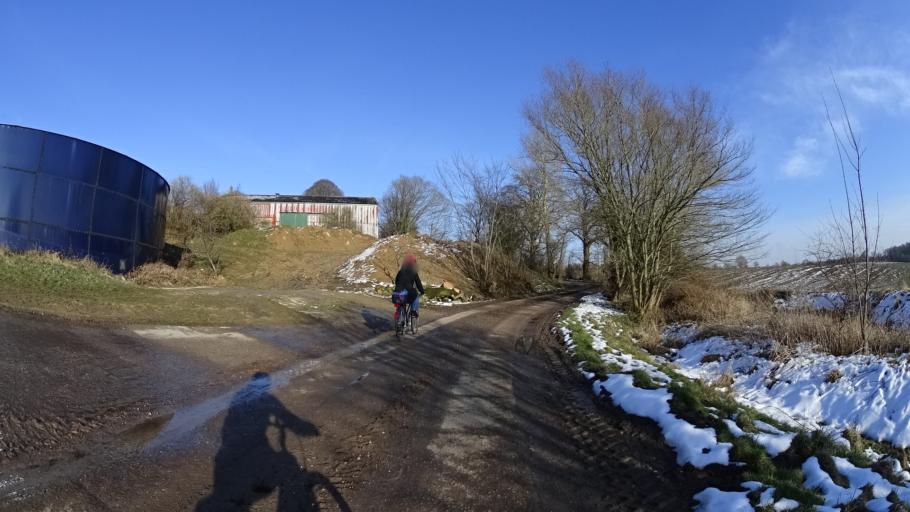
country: DE
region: Schleswig-Holstein
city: Martensrade
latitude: 54.2786
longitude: 10.3810
